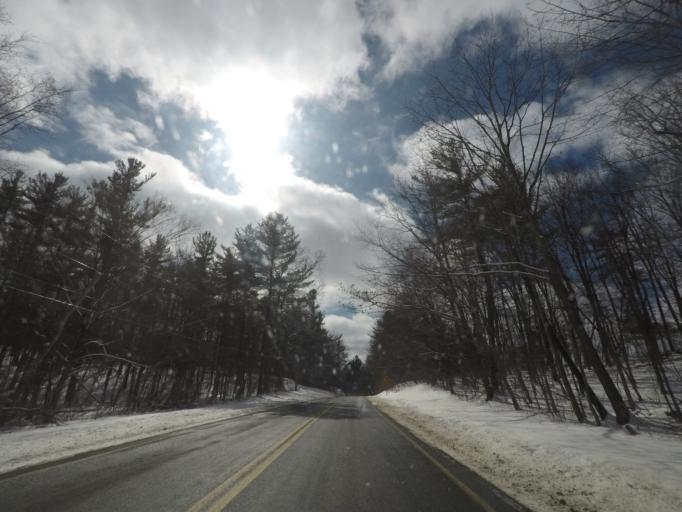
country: US
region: New York
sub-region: Columbia County
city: Chatham
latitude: 42.4099
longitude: -73.5516
